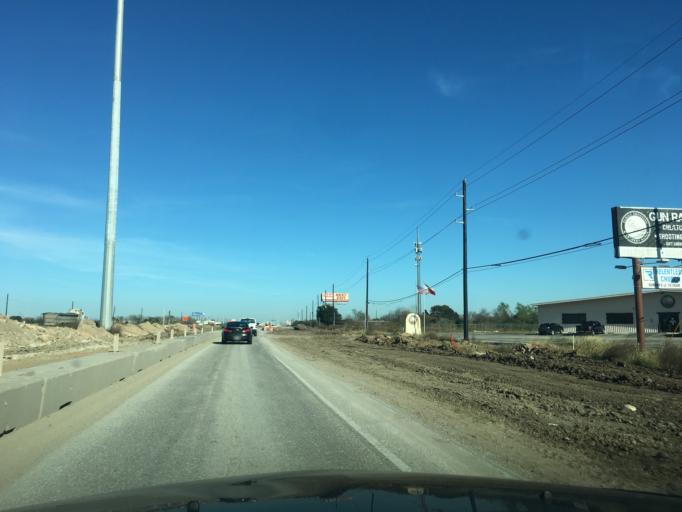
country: US
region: Texas
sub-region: Fort Bend County
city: Rosenberg
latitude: 29.5367
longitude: -95.7690
